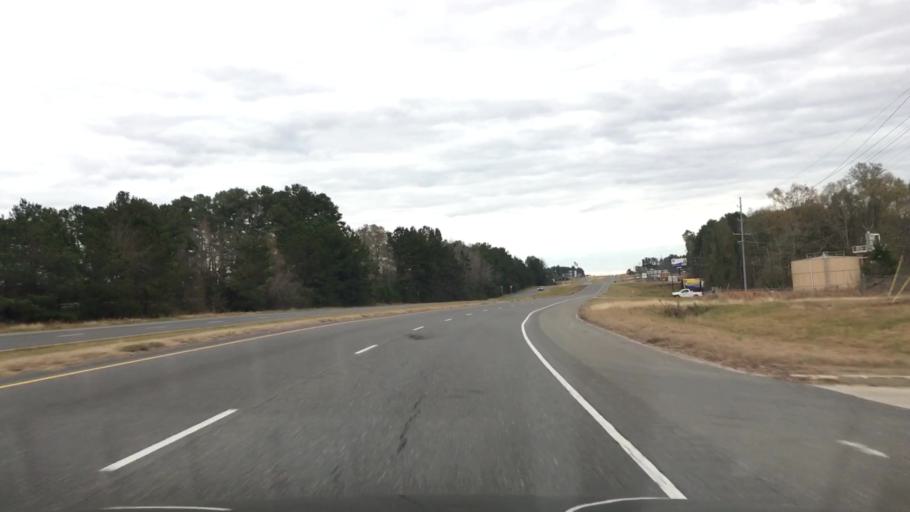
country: US
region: Louisiana
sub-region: Vernon Parish
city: New Llano
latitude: 31.0996
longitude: -93.2693
